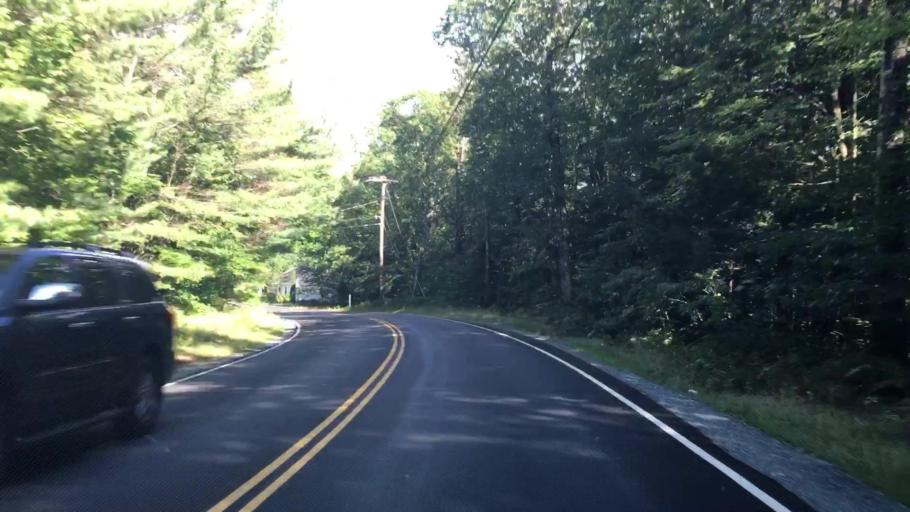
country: US
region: New Hampshire
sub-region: Grafton County
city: Woodstock
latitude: 44.0291
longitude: -71.7068
